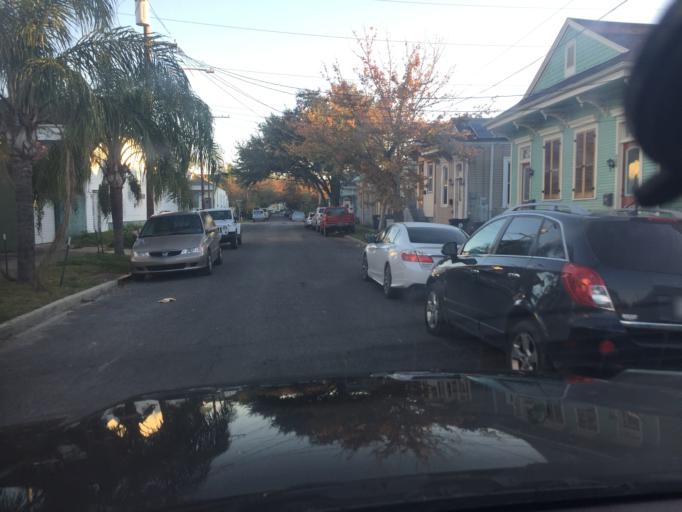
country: US
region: Louisiana
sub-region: Orleans Parish
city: New Orleans
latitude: 29.9731
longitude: -90.0843
